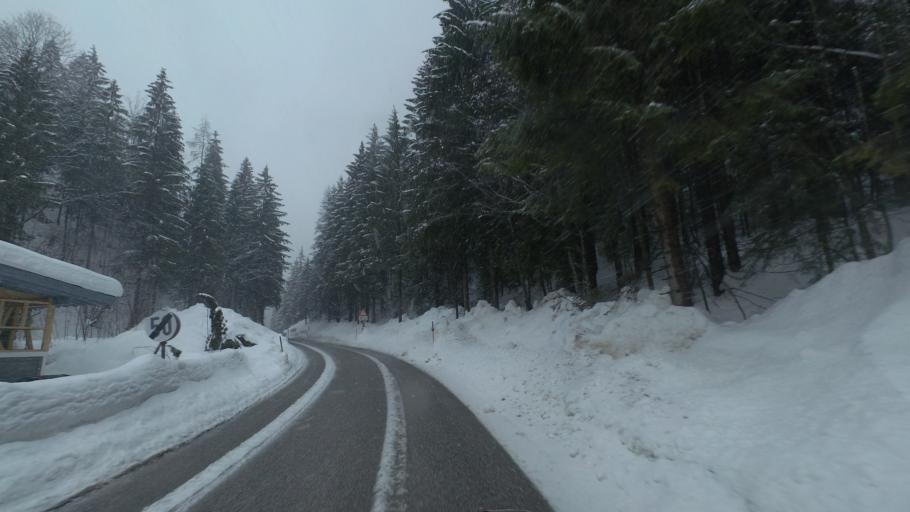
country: AT
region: Tyrol
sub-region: Politischer Bezirk Kitzbuhel
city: Kossen
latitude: 47.6784
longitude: 12.3995
